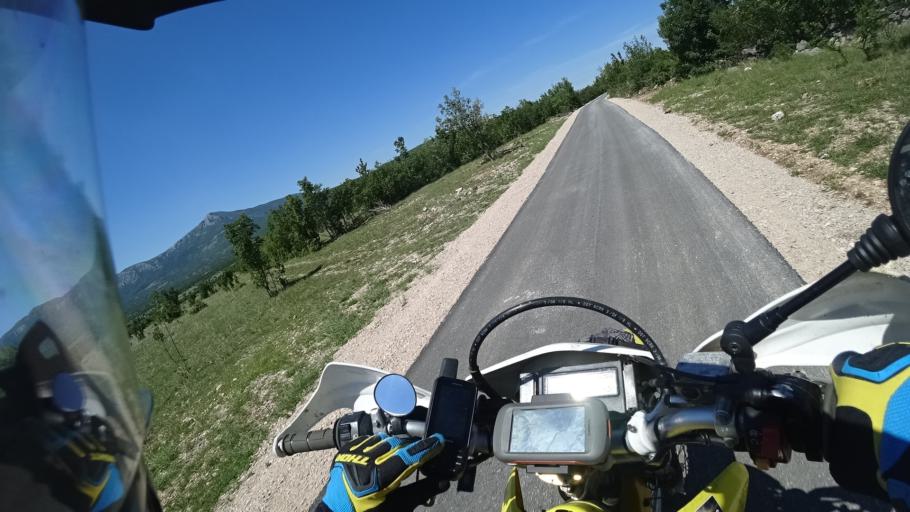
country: BA
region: Federation of Bosnia and Herzegovina
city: Bosansko Grahovo
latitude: 44.0041
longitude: 16.3830
